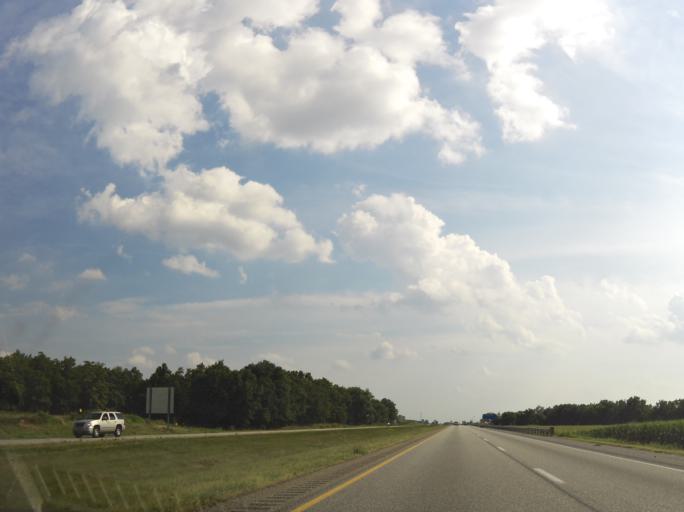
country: US
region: Pennsylvania
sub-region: Franklin County
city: Greencastle
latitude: 39.7685
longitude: -77.7210
